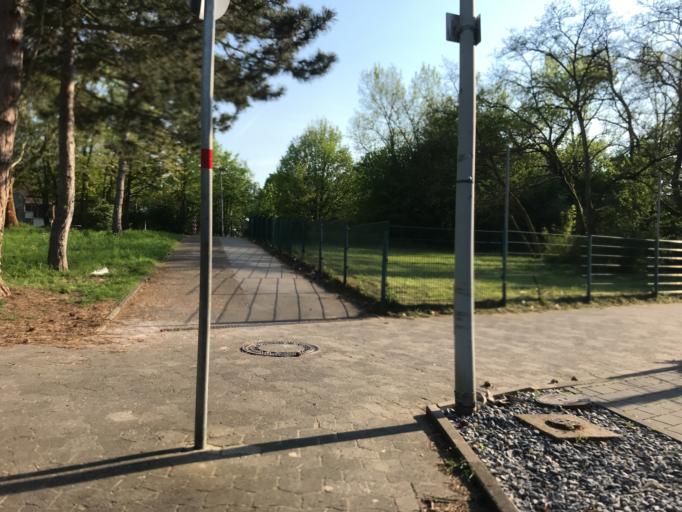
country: DE
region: Rheinland-Pfalz
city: Budenheim
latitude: 50.0184
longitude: 8.2172
